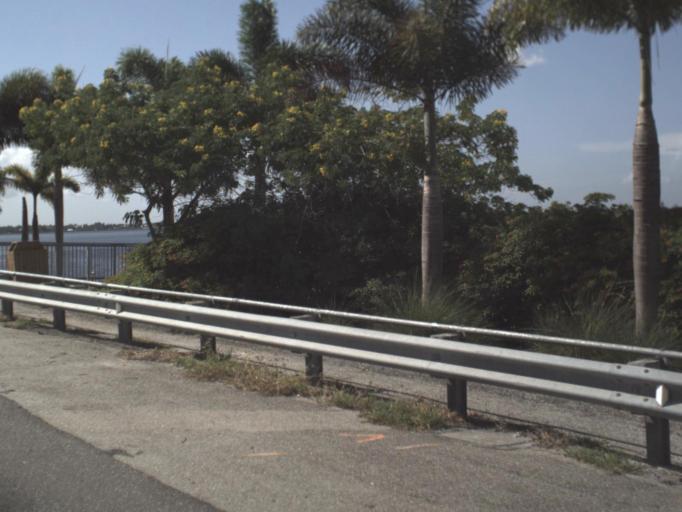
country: US
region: Florida
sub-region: Charlotte County
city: Charlotte Harbor
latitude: 26.9528
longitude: -82.0625
